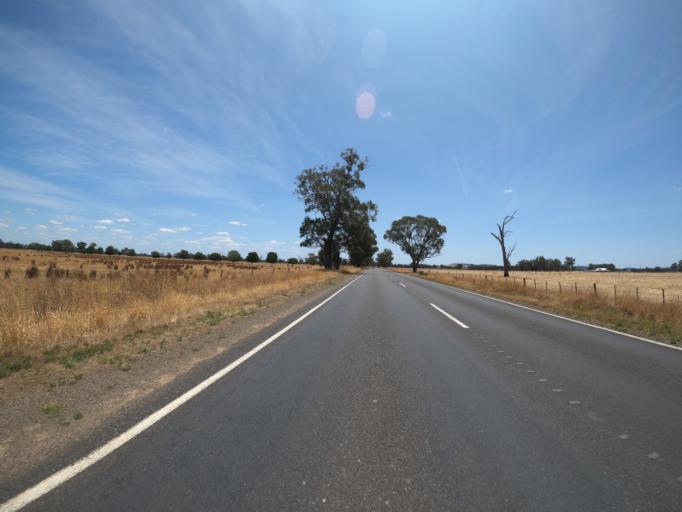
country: AU
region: Victoria
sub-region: Benalla
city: Benalla
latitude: -36.5152
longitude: 146.0314
